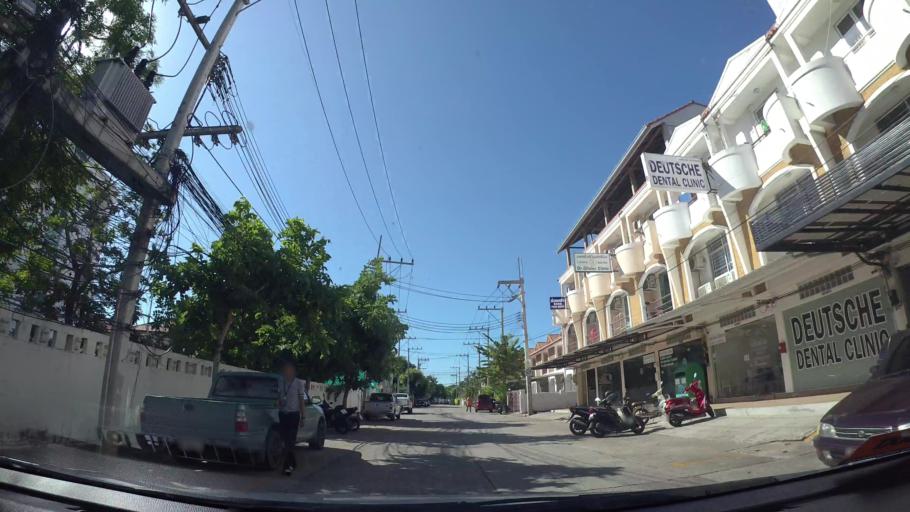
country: TH
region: Chon Buri
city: Phatthaya
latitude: 12.9063
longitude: 100.8739
